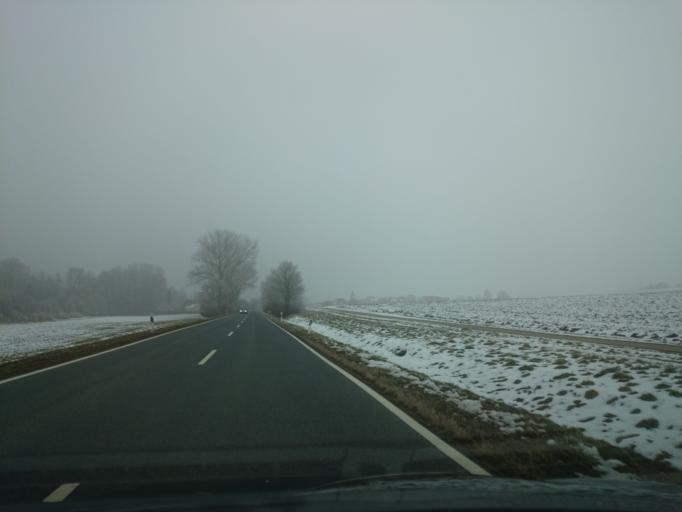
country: DE
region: Bavaria
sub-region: Regierungsbezirk Mittelfranken
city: Thalmassing
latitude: 49.1161
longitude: 11.2738
